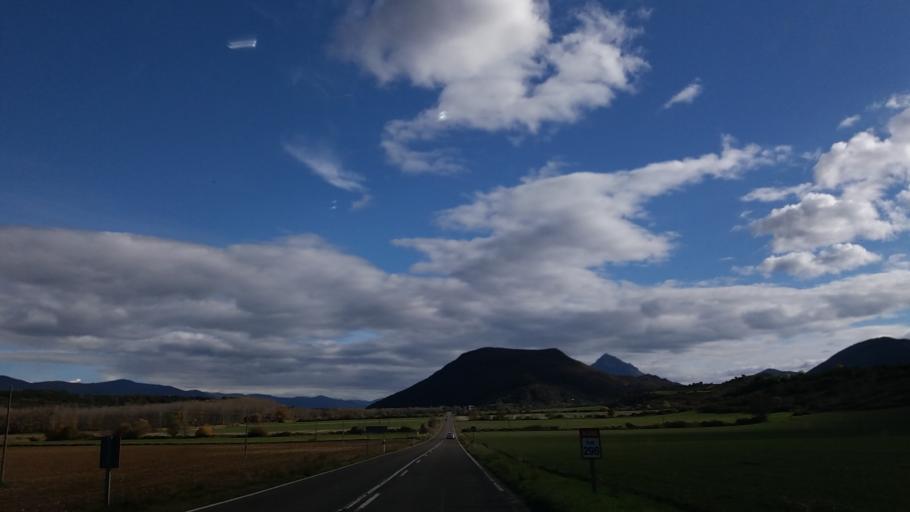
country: ES
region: Aragon
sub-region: Provincia de Huesca
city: Santa Cruz de la Seros
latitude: 42.5568
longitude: -0.7015
